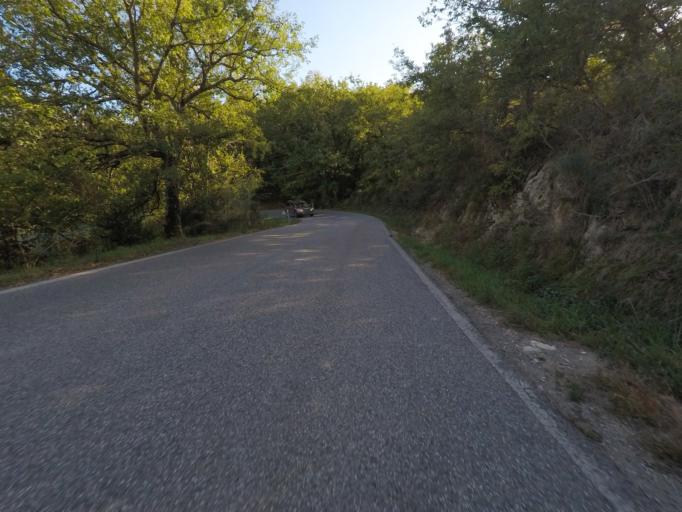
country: IT
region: Tuscany
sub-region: Provincia di Siena
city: Radda in Chianti
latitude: 43.4784
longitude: 11.3698
